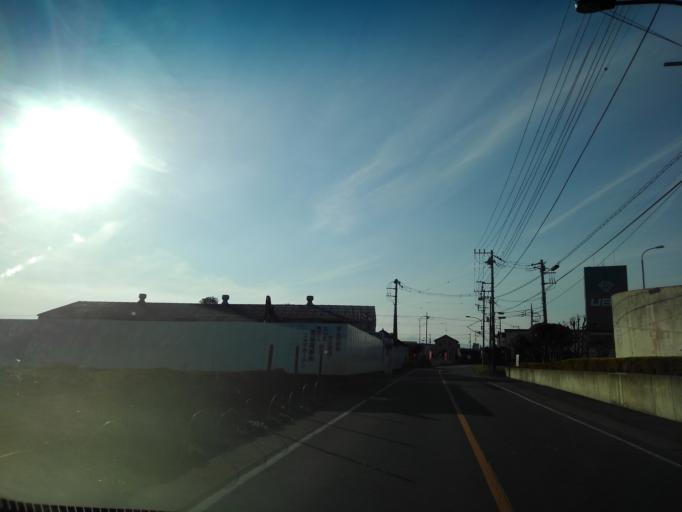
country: JP
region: Tokyo
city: Fussa
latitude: 35.7915
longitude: 139.3655
